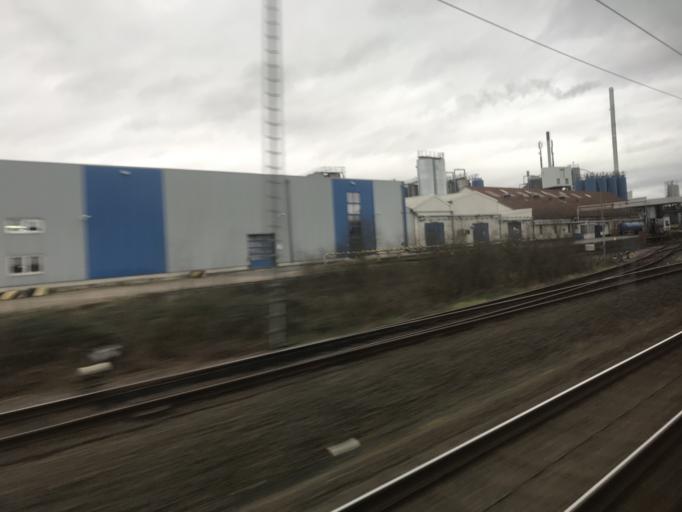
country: DE
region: Lower Saxony
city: Dollbergen
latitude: 52.4150
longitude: 10.1734
